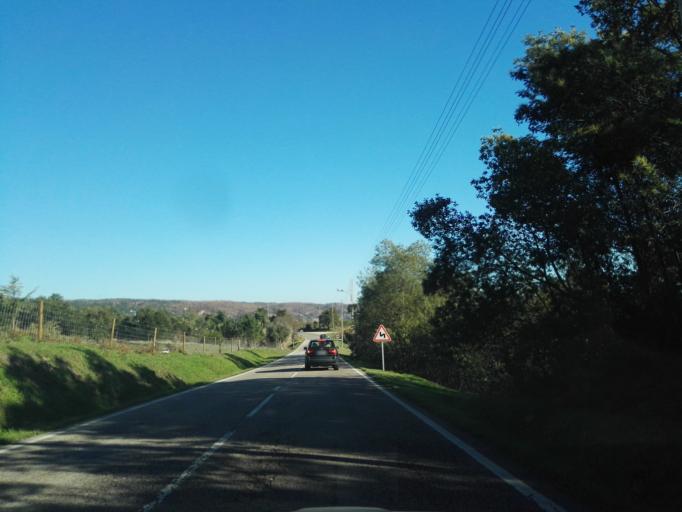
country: PT
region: Santarem
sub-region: Abrantes
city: Tramagal
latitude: 39.4818
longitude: -8.2846
